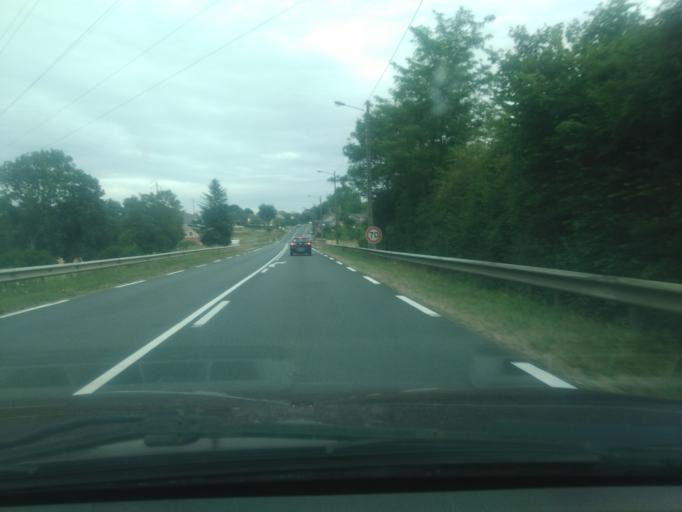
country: FR
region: Centre
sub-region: Departement de l'Indre
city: La Chatre
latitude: 46.5766
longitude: 1.9631
